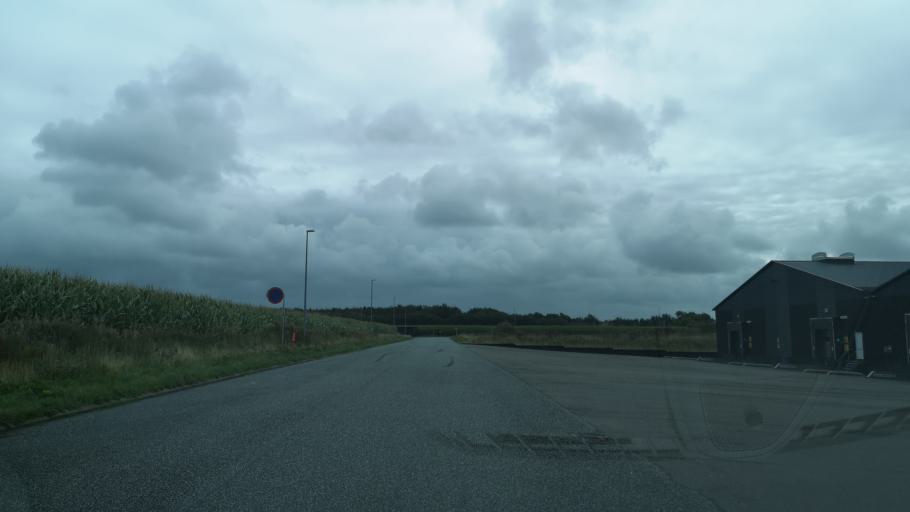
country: DK
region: Central Jutland
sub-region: Ringkobing-Skjern Kommune
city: Videbaek
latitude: 56.0879
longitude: 8.6422
